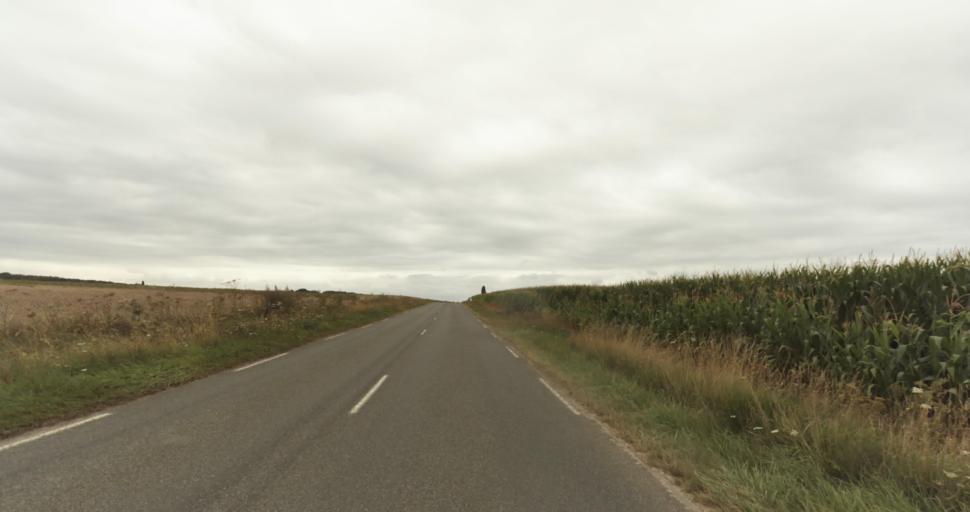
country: FR
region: Haute-Normandie
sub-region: Departement de l'Eure
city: Gravigny
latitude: 49.0524
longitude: 1.2336
